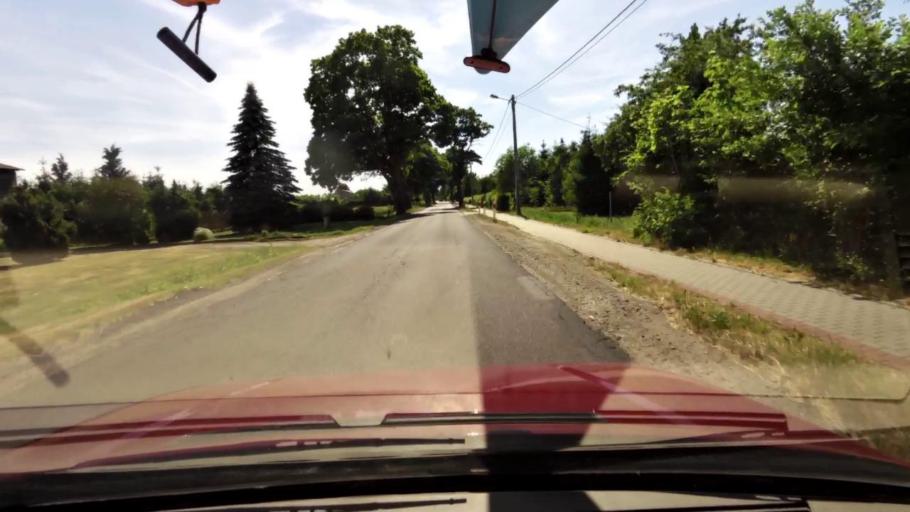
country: PL
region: Pomeranian Voivodeship
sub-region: Powiat slupski
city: Kobylnica
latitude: 54.3962
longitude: 16.9889
